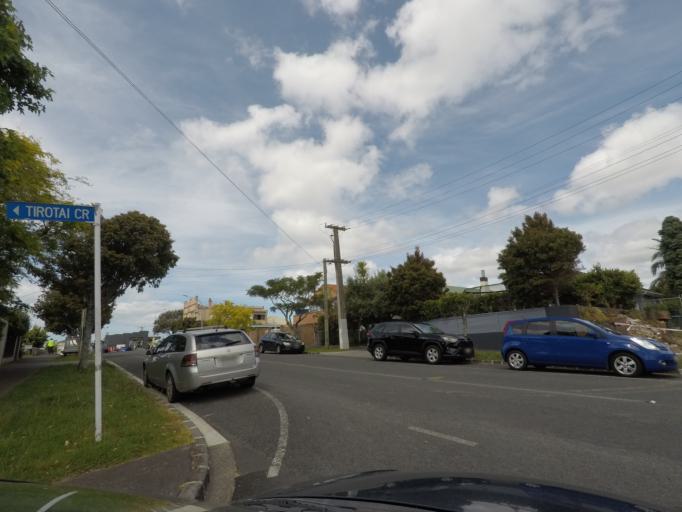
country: NZ
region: Auckland
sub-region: Auckland
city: Auckland
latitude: -36.8542
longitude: 174.7170
